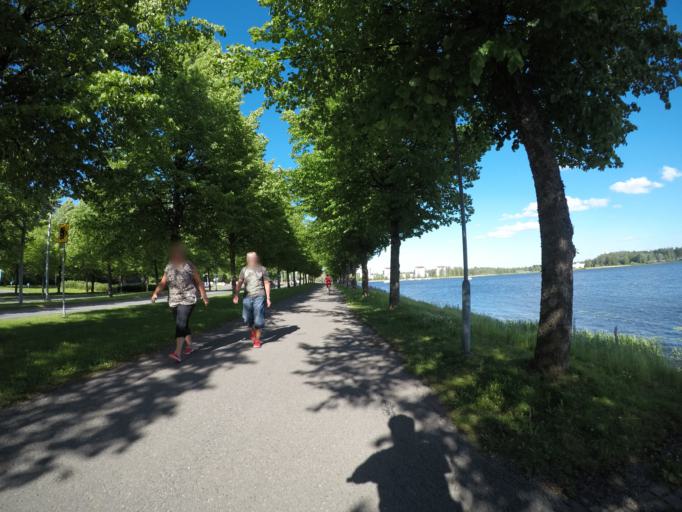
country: FI
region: Haeme
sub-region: Haemeenlinna
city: Haemeenlinna
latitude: 60.9942
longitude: 24.4691
